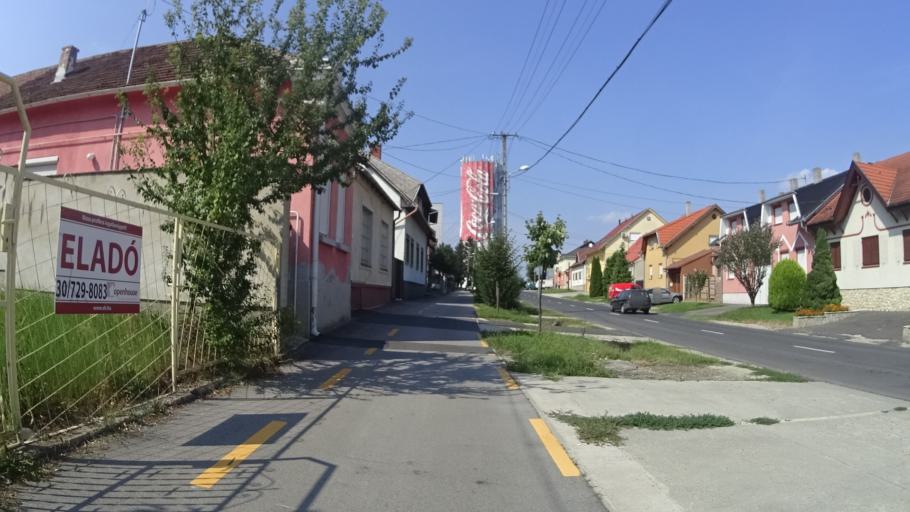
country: HU
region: Zala
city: Nagykanizsa
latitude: 46.4619
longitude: 16.9988
